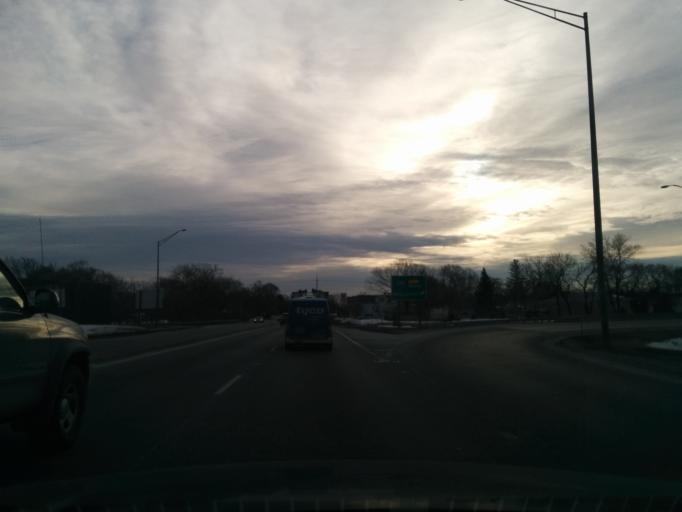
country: US
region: Illinois
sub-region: Cook County
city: Schiller Park
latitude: 41.9566
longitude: -87.8793
